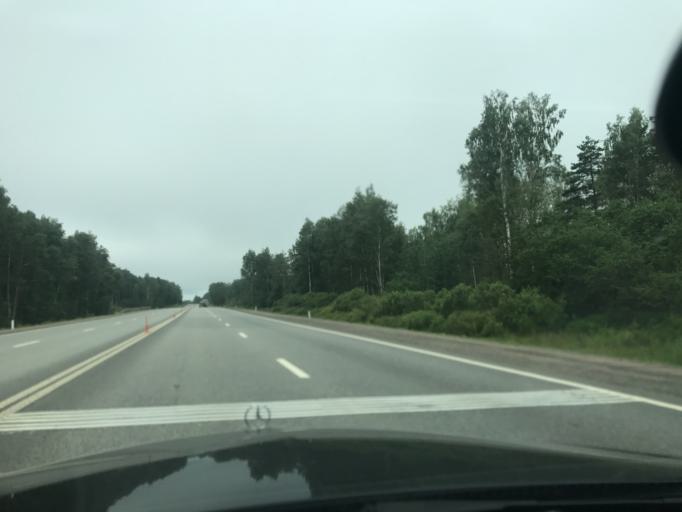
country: RU
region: Smolensk
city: Vyaz'ma
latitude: 55.2933
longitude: 34.4699
